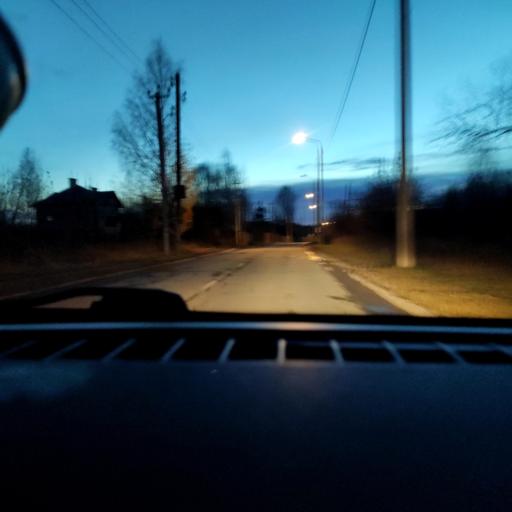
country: RU
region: Perm
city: Perm
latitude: 58.0271
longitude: 56.1907
